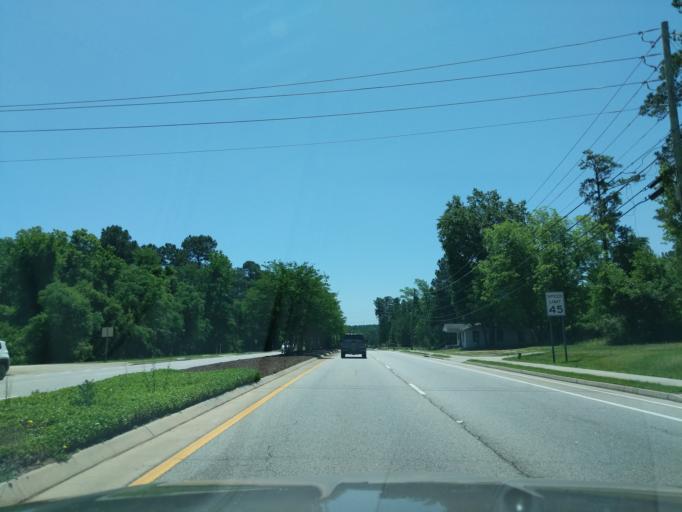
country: US
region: Georgia
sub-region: Columbia County
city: Martinez
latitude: 33.5487
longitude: -82.0891
